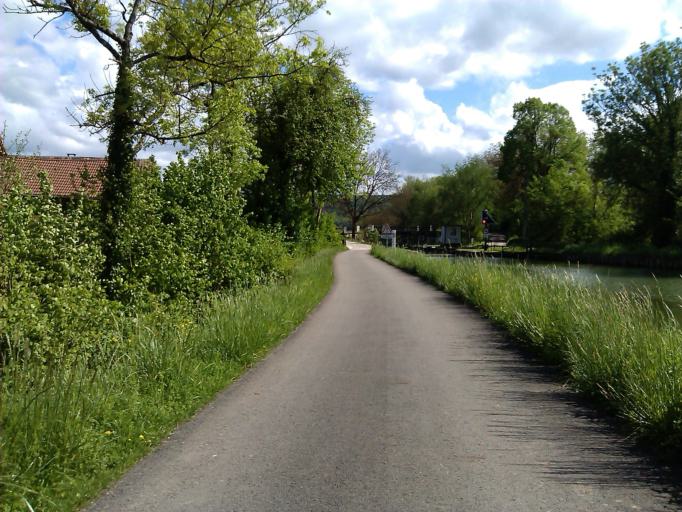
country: FR
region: Franche-Comte
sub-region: Departement du Doubs
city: Colombier-Fontaine
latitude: 47.4393
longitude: 6.6282
